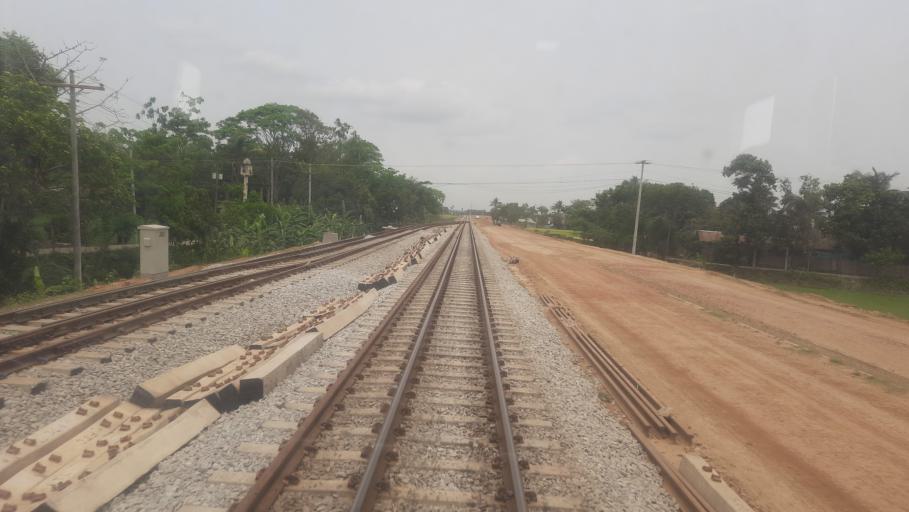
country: BD
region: Chittagong
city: Comilla
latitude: 23.5832
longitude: 91.1510
